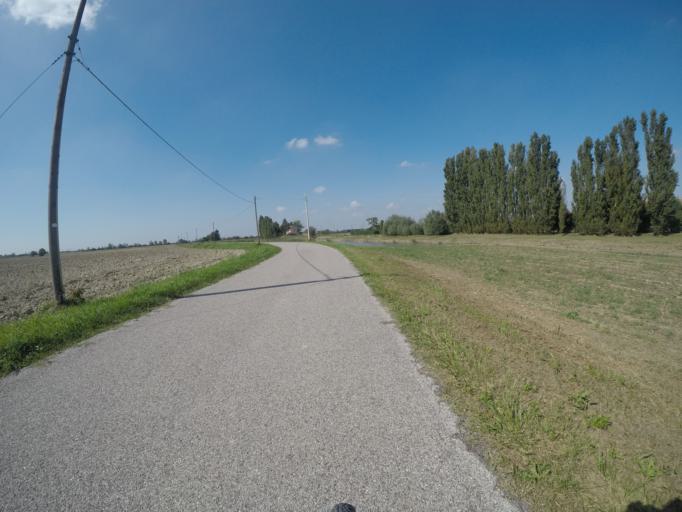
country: IT
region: Veneto
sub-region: Provincia di Rovigo
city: Polesella
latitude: 44.9788
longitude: 11.7557
